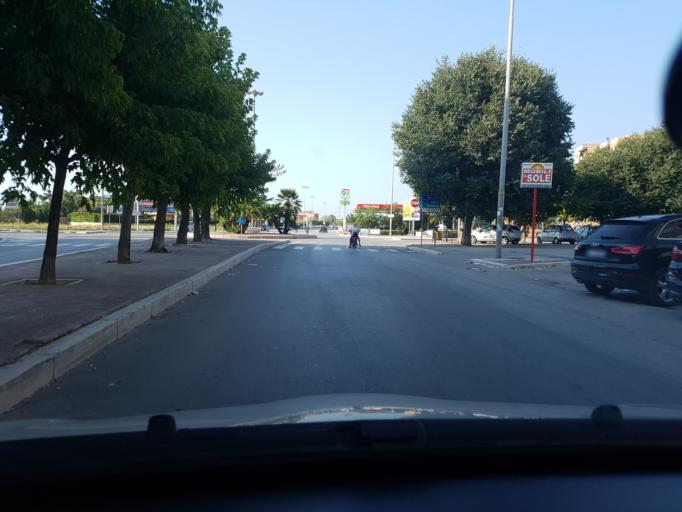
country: IT
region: Apulia
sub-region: Provincia di Foggia
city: Cerignola
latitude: 41.2656
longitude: 15.9090
